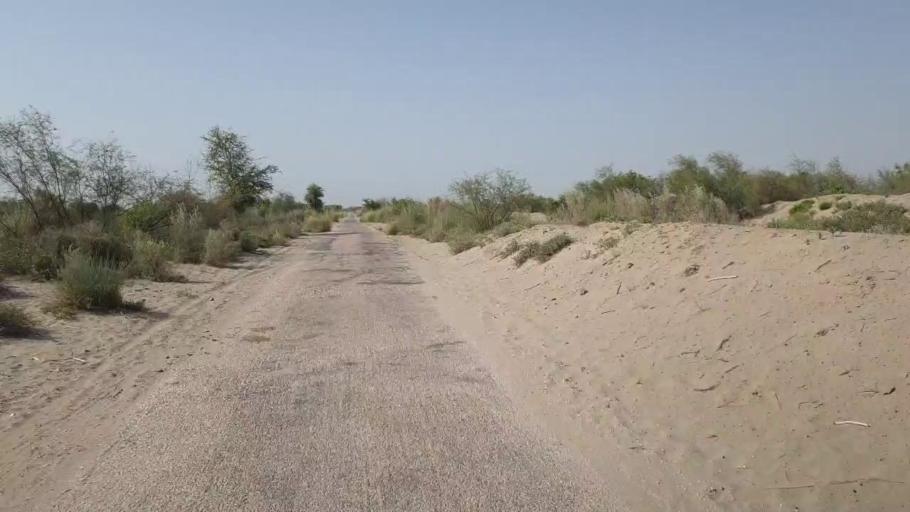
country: PK
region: Sindh
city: Jam Sahib
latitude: 26.5875
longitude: 68.9215
